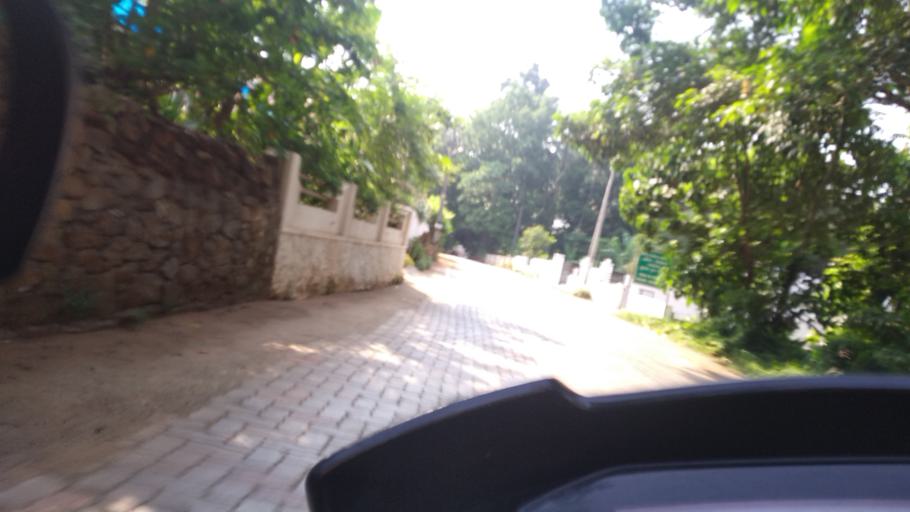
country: IN
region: Kerala
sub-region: Ernakulam
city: Piravam
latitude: 9.8540
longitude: 76.5275
